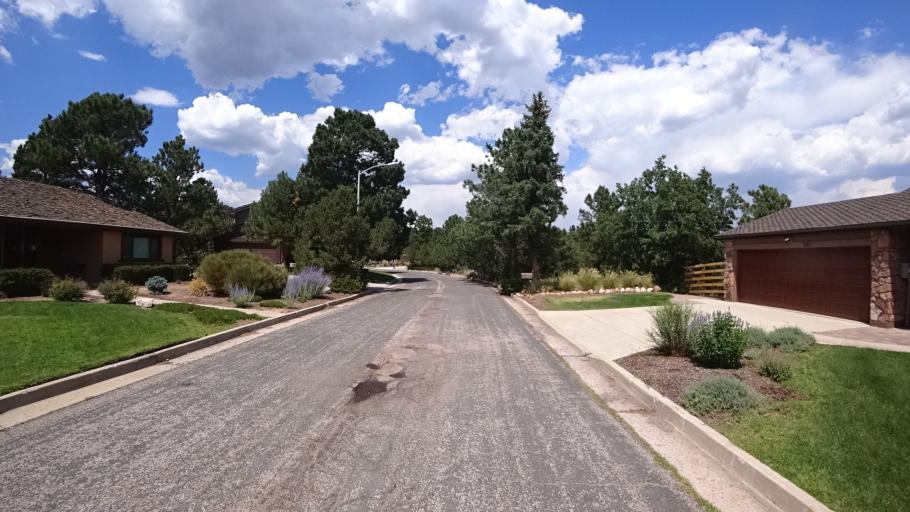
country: US
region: Colorado
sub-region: El Paso County
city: Air Force Academy
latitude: 38.9321
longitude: -104.8246
